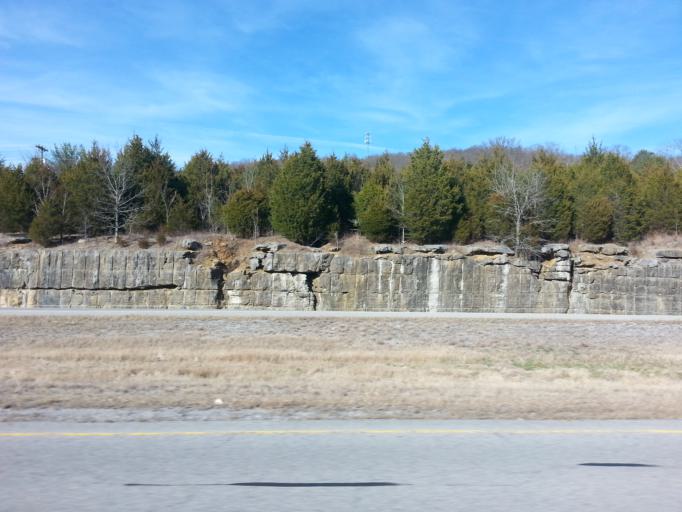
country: US
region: Tennessee
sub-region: Cannon County
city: Woodbury
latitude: 35.8097
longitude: -86.2082
